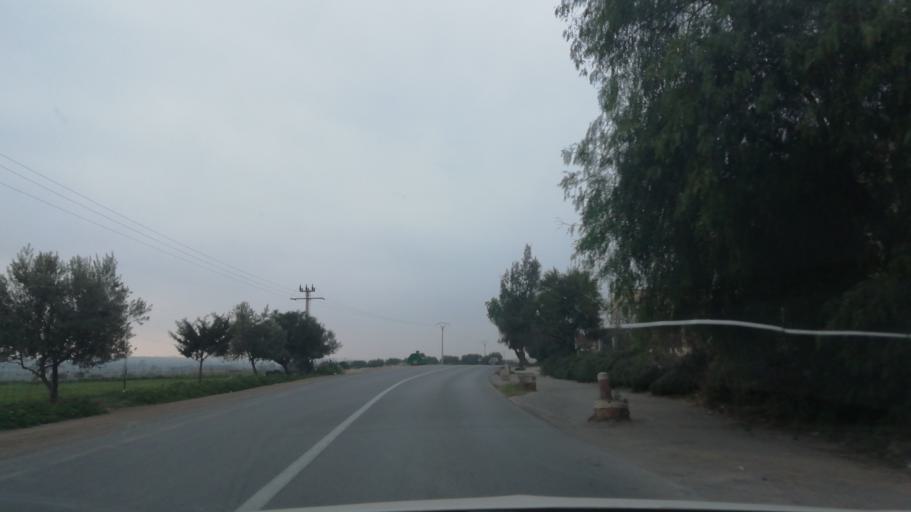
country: DZ
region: Sidi Bel Abbes
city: Sfizef
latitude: 35.2535
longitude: -0.1915
